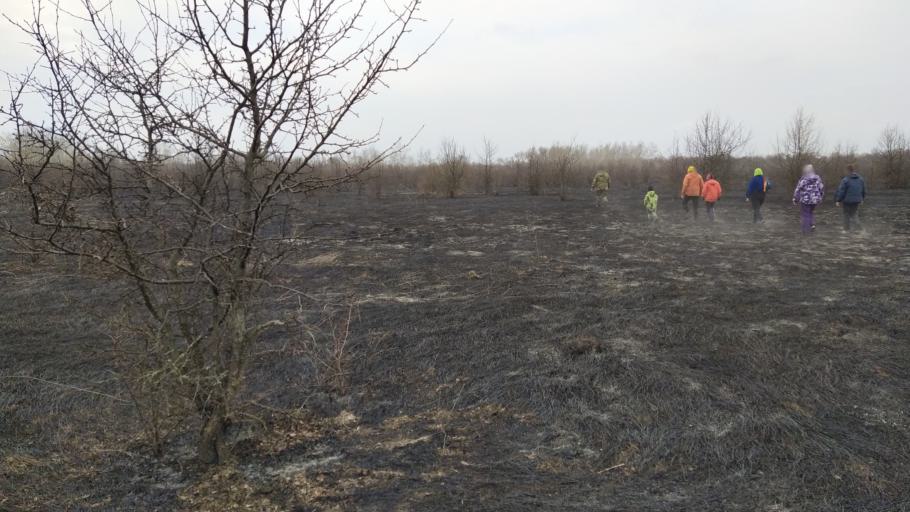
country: RU
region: Rostov
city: Semikarakorsk
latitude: 47.5433
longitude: 40.6843
